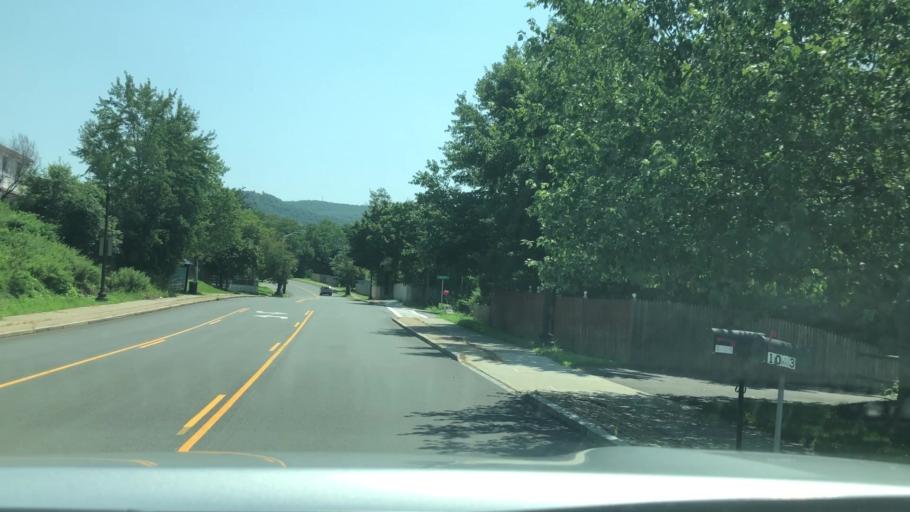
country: US
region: New York
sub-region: Dutchess County
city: Beacon
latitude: 41.5016
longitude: -73.9806
